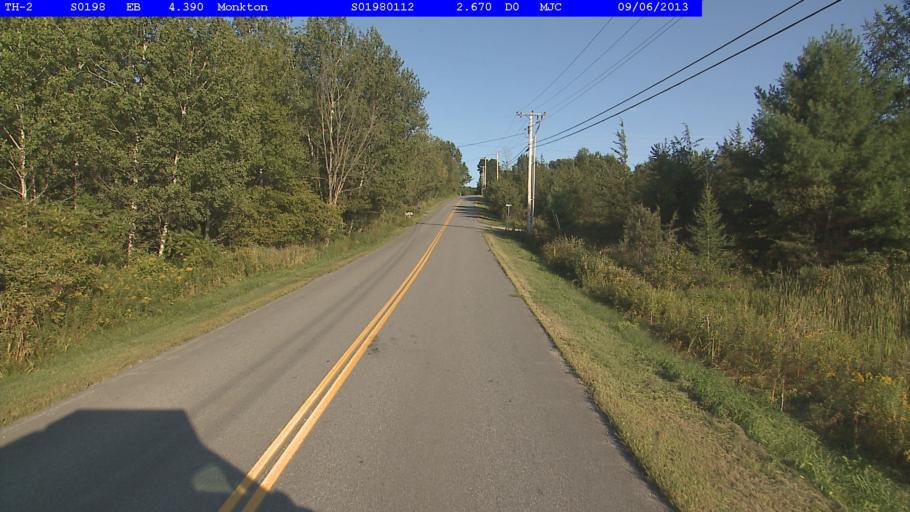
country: US
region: Vermont
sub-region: Chittenden County
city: Hinesburg
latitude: 44.2388
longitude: -73.1511
